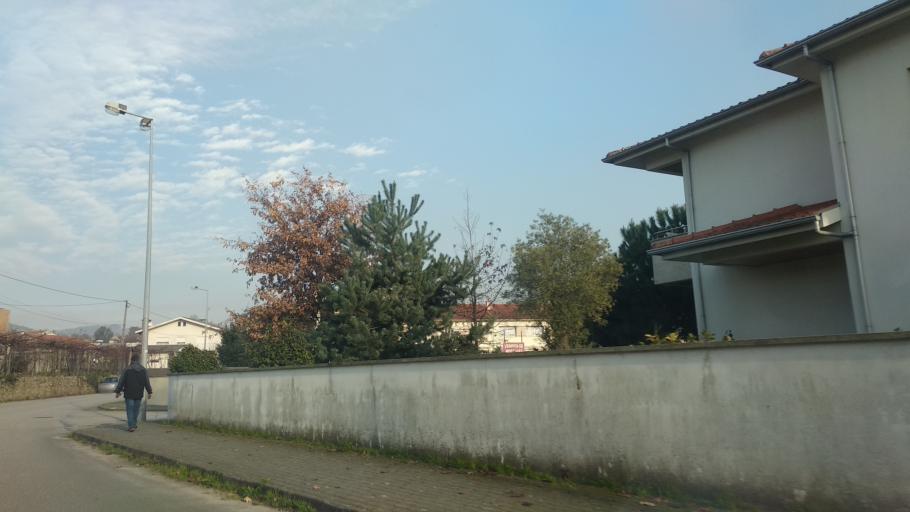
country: PT
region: Braga
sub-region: Braga
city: Adaufe
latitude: 41.5643
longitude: -8.3836
